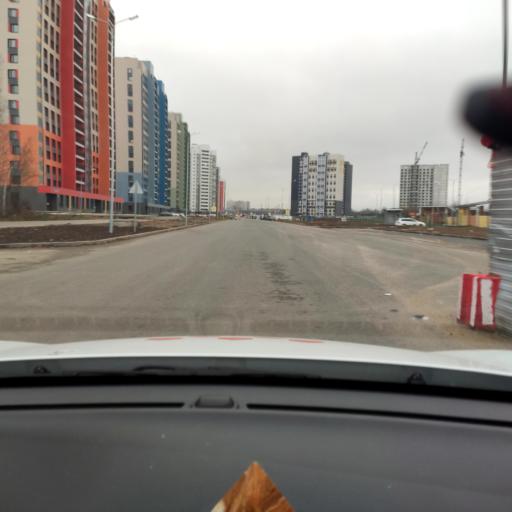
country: RU
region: Tatarstan
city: Osinovo
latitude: 55.8560
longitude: 48.9086
